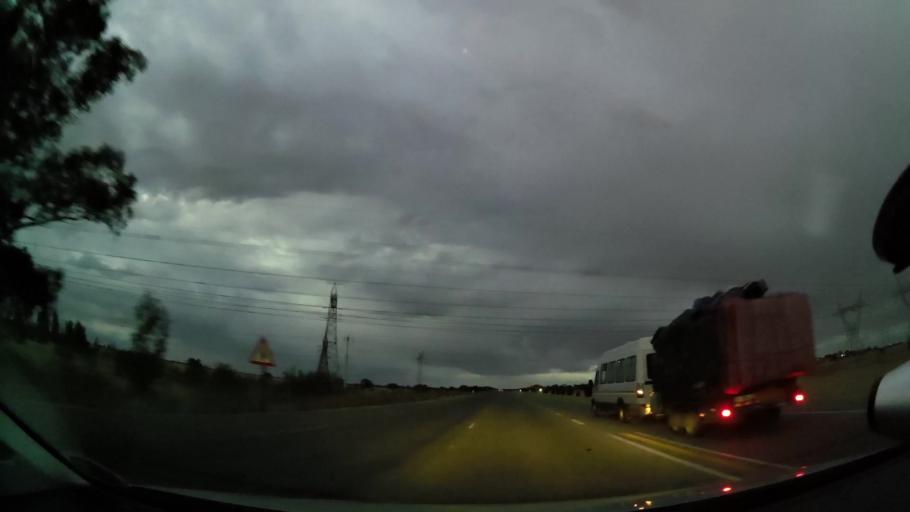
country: ZA
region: Orange Free State
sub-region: Lejweleputswa District Municipality
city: Welkom
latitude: -27.9328
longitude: 26.7860
